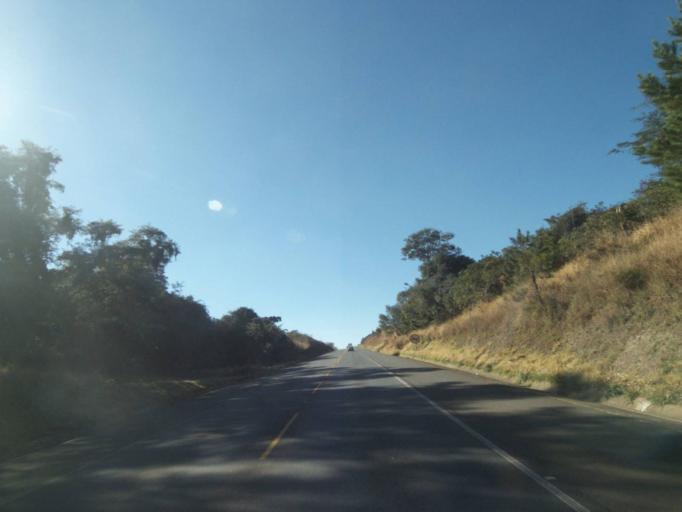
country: BR
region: Parana
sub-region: Tibagi
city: Tibagi
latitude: -24.6051
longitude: -50.4404
